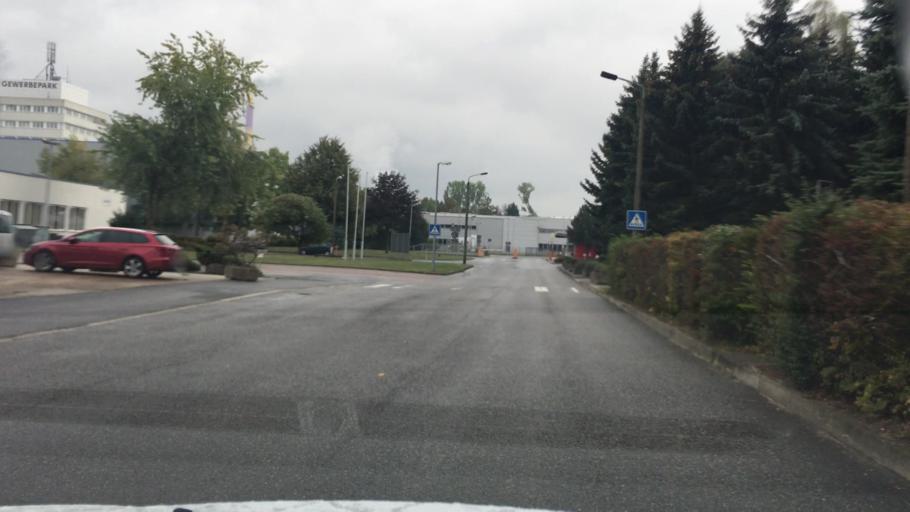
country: DE
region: Saxony
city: Wittgensdorf
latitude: 50.8692
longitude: 12.9055
